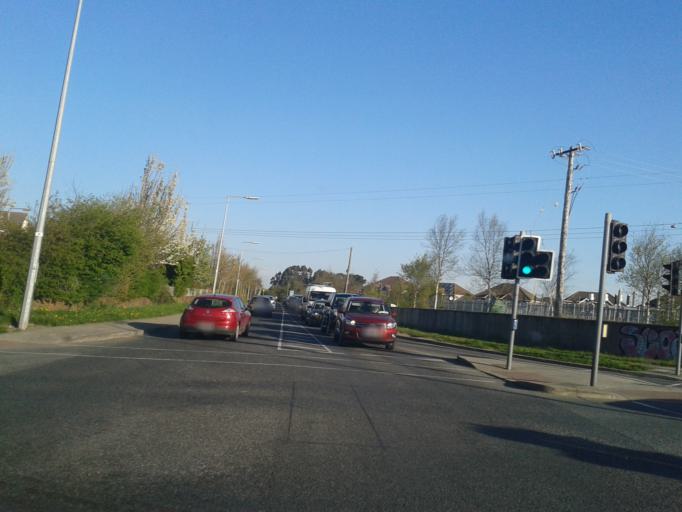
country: IE
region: Leinster
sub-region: Fingal County
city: Swords
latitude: 53.4670
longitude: -6.2384
